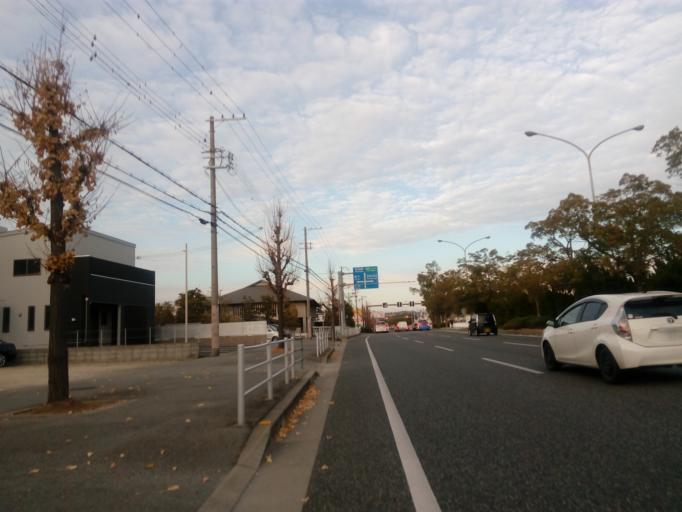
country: JP
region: Hyogo
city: Himeji
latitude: 34.7994
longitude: 134.6784
